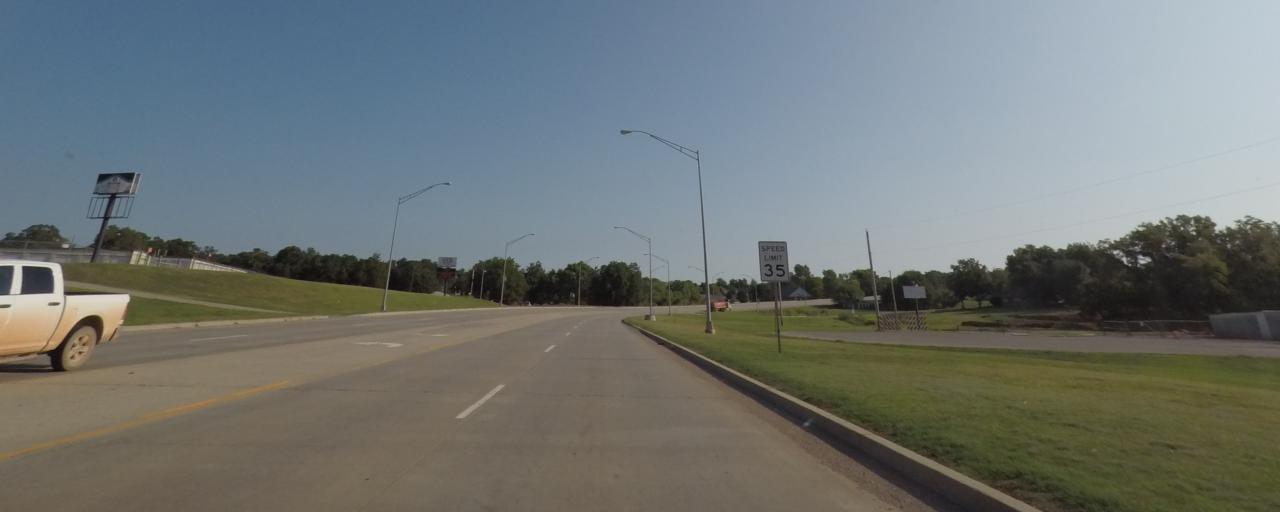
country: US
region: Oklahoma
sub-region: McClain County
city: Blanchard
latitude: 35.1351
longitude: -97.6643
